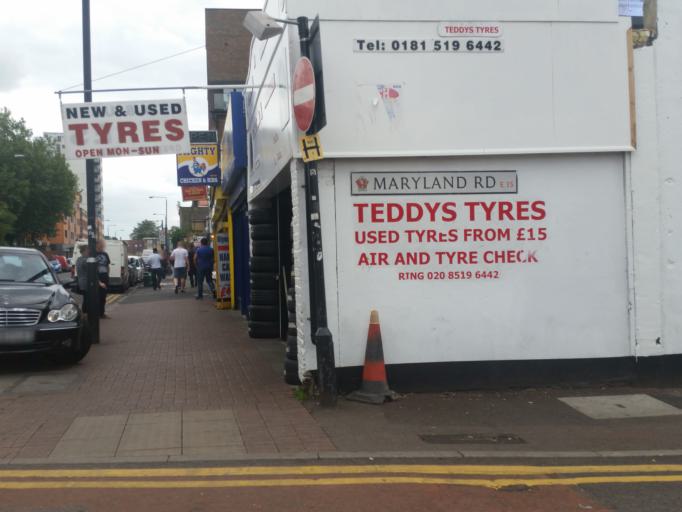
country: GB
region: England
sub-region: Greater London
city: Poplar
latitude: 51.5484
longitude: 0.0053
